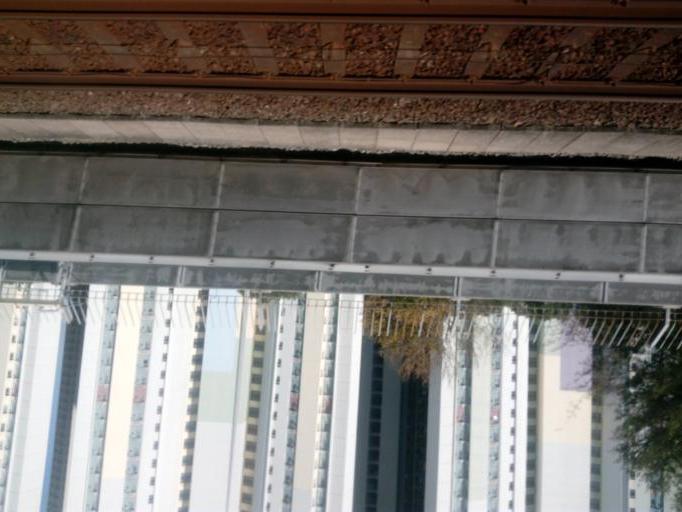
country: HK
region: Sha Tin
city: Sha Tin
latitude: 22.4068
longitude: 114.2217
